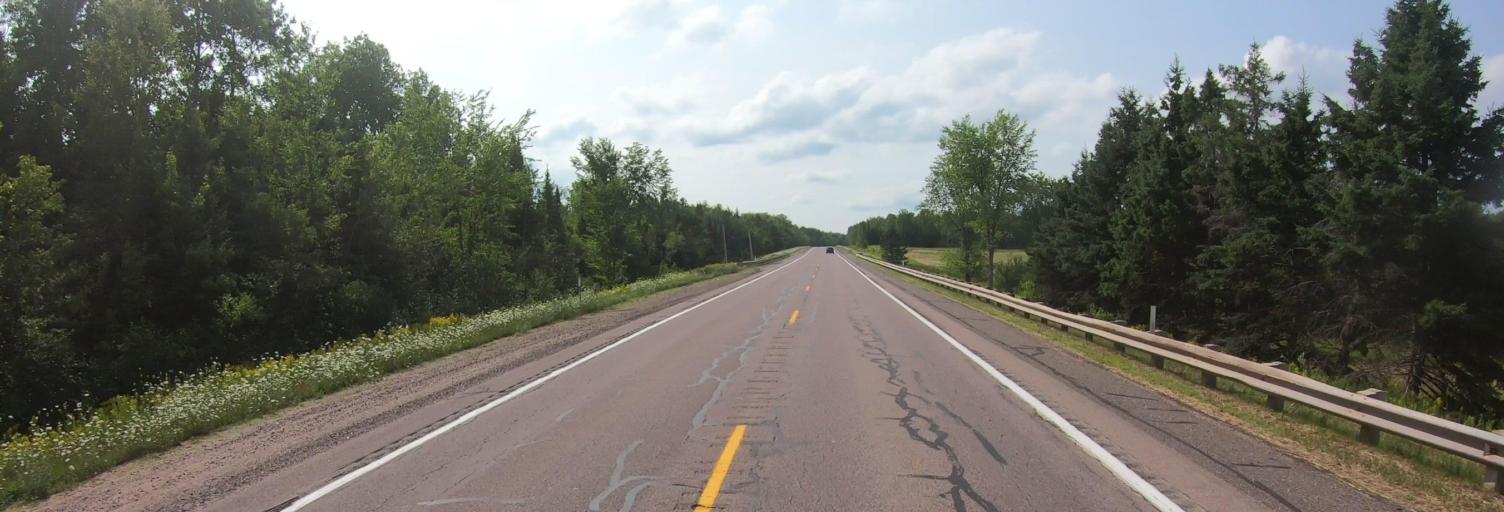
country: US
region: Michigan
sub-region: Ontonagon County
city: Ontonagon
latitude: 46.5777
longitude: -89.4998
